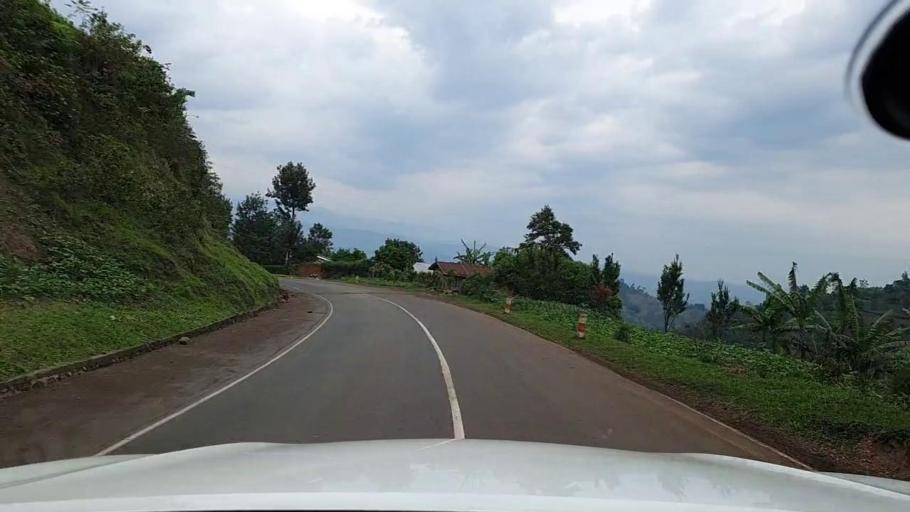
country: RW
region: Western Province
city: Cyangugu
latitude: -2.6595
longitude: 28.9730
